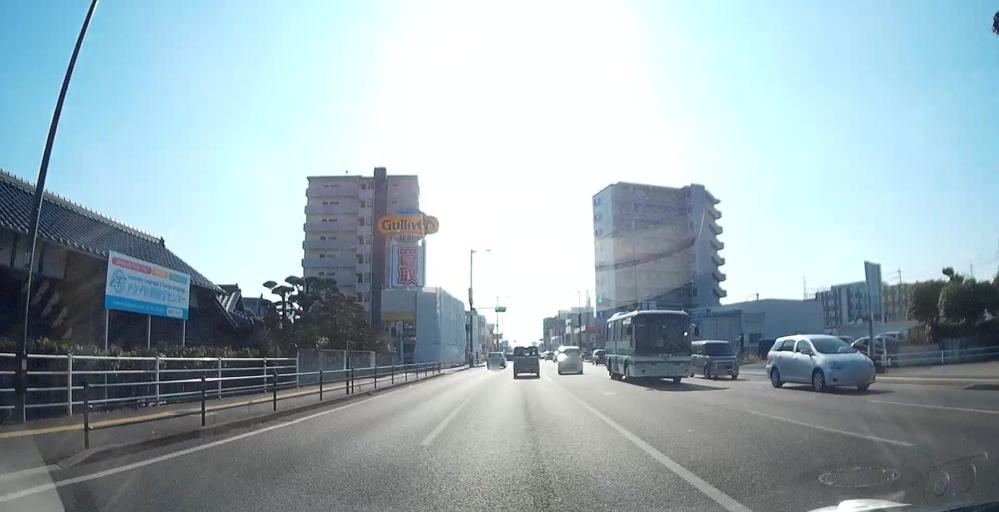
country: JP
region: Kumamoto
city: Kumamoto
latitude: 32.7708
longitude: 130.6938
